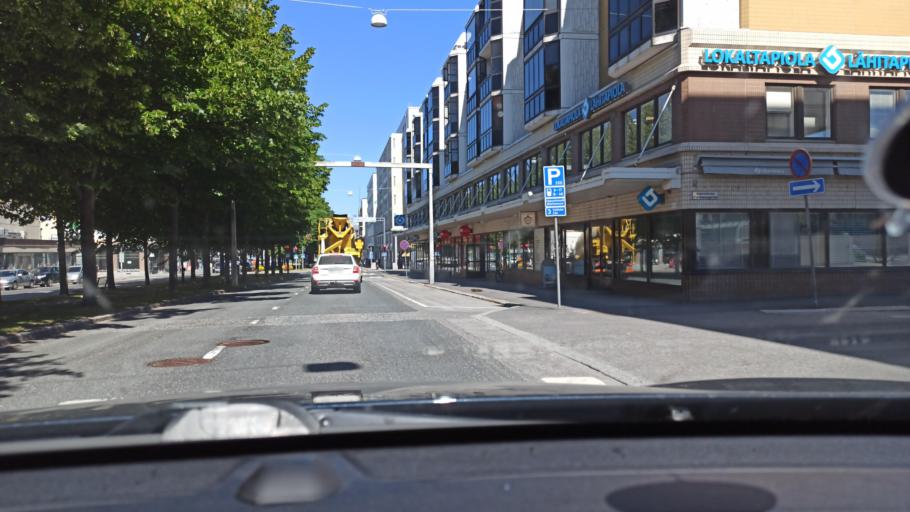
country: FI
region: Ostrobothnia
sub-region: Vaasa
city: Vaasa
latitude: 63.0929
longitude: 21.6187
